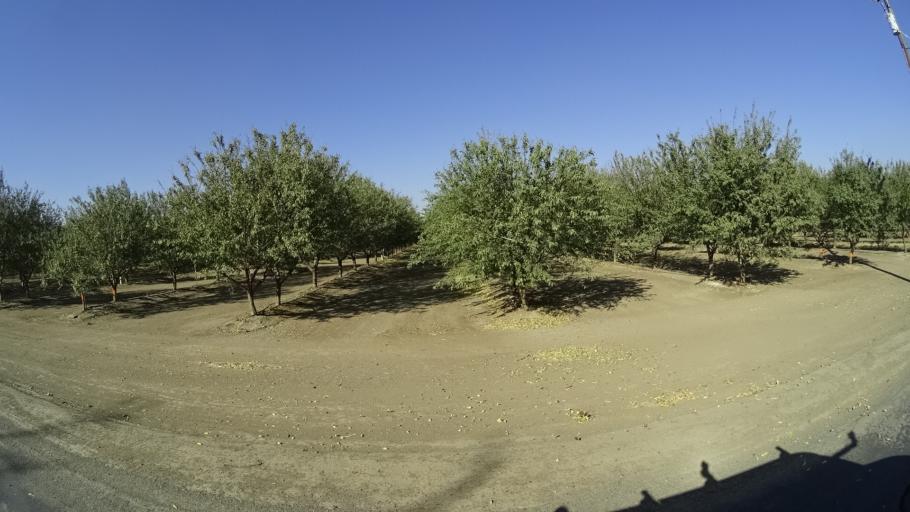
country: US
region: California
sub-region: Yolo County
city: Woodland
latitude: 38.7497
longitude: -121.7894
